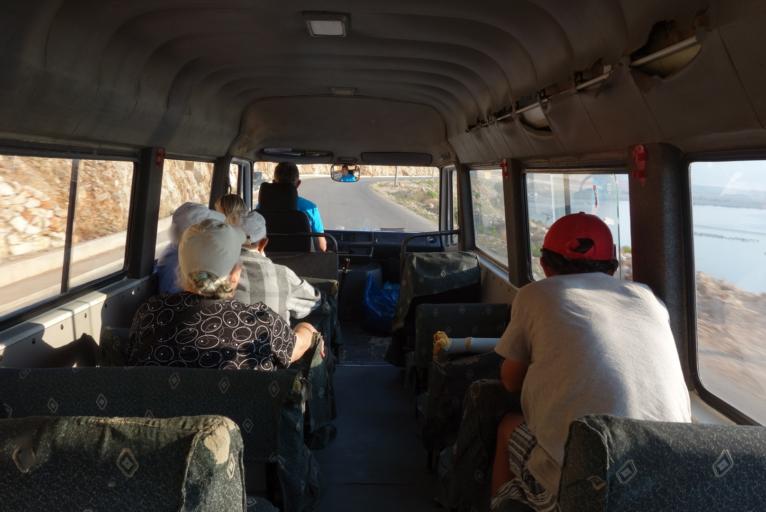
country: AL
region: Vlore
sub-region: Rrethi i Sarandes
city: Sarande
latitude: 39.7999
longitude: 20.0121
